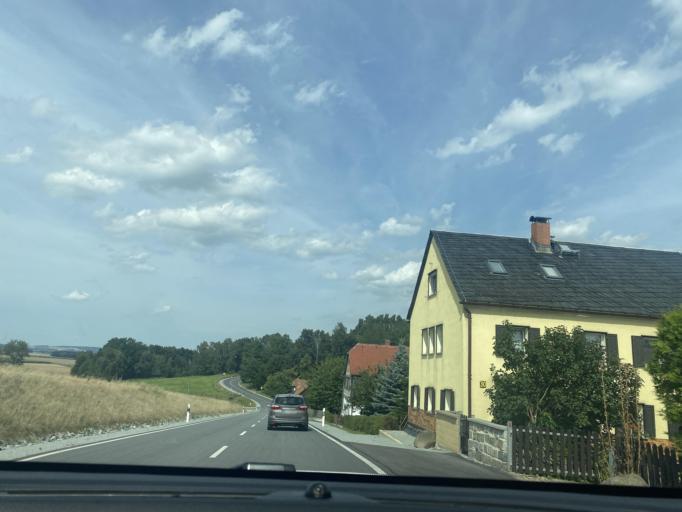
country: DE
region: Saxony
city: Herrnhut
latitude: 50.9624
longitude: 14.7375
